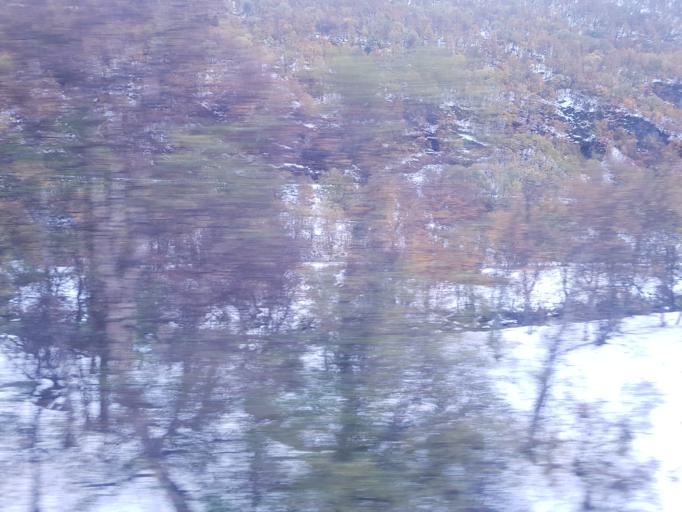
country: NO
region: Sor-Trondelag
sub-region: Oppdal
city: Oppdal
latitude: 62.4040
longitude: 9.6313
